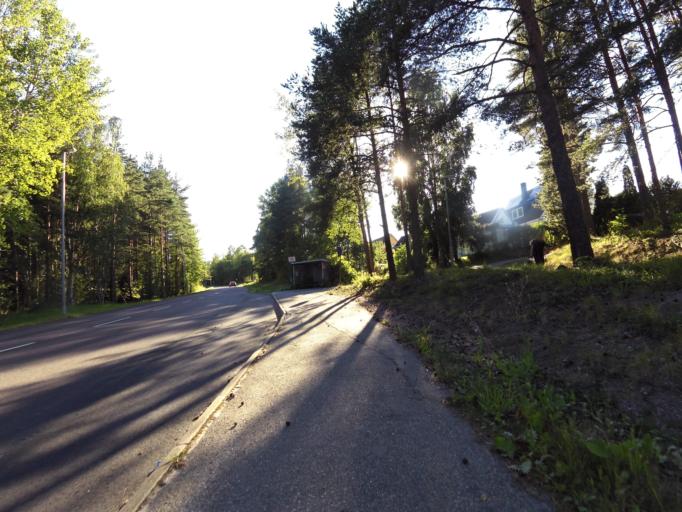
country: SE
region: Gaevleborg
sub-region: Gavle Kommun
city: Gavle
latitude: 60.6499
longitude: 17.1484
